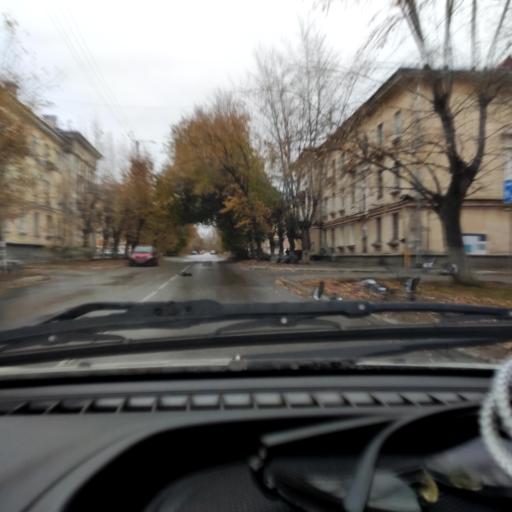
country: RU
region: Samara
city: Zhigulevsk
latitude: 53.4654
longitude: 49.5309
